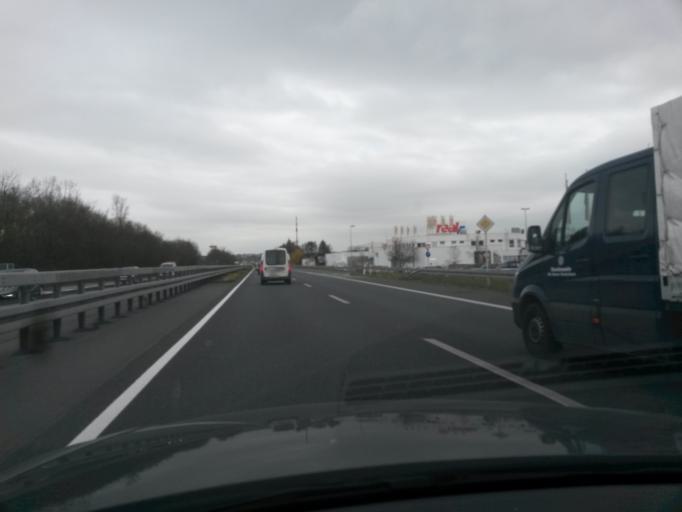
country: DE
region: Bavaria
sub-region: Regierungsbezirk Unterfranken
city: Wuerzburg
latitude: 49.8112
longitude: 9.9746
